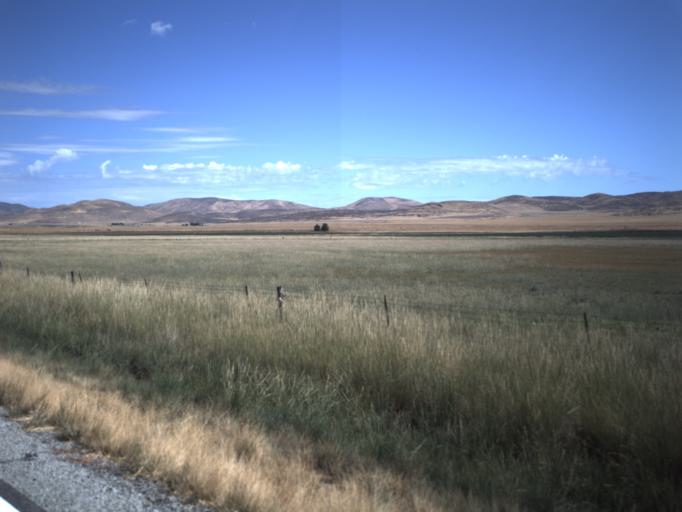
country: US
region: Utah
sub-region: Box Elder County
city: Tremonton
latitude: 41.7587
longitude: -112.4348
